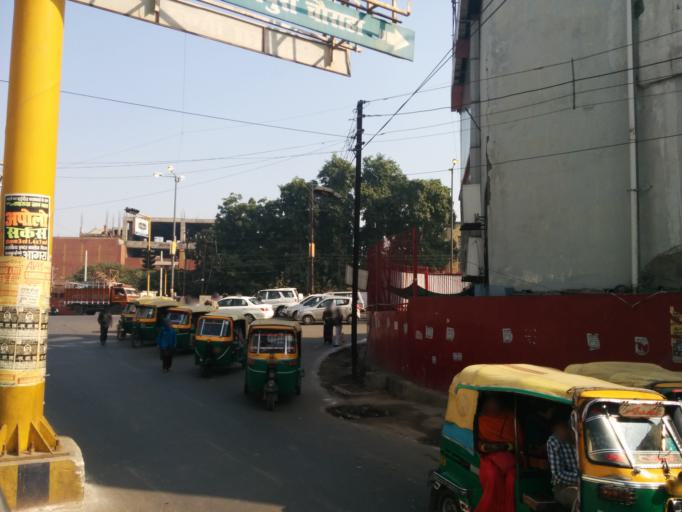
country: IN
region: Uttar Pradesh
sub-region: Agra
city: Agra
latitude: 27.1703
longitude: 78.0091
